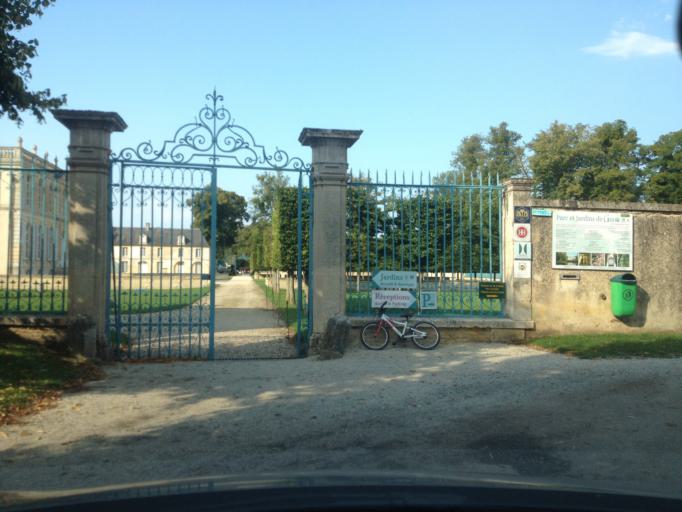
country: FR
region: Lower Normandy
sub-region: Departement du Calvados
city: Canon
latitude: 49.0778
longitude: -0.0946
